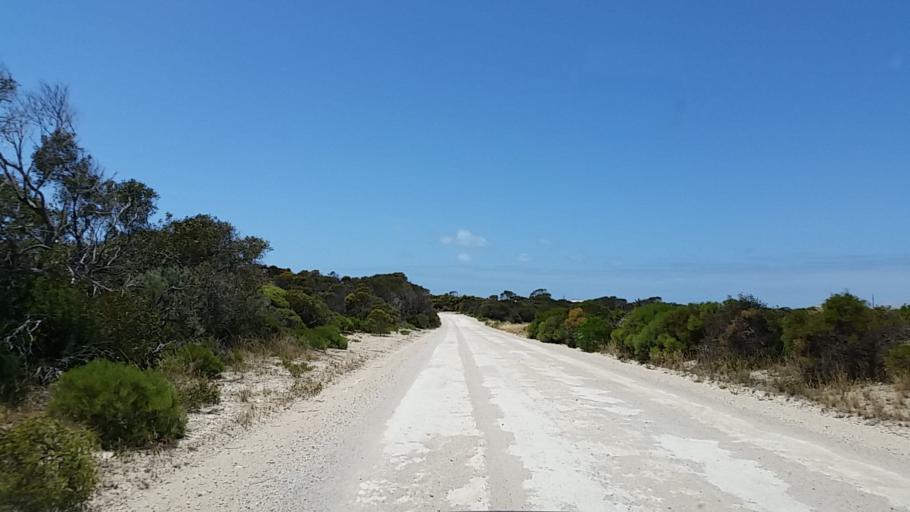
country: AU
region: South Australia
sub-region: Yorke Peninsula
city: Honiton
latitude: -35.2294
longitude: 137.1196
